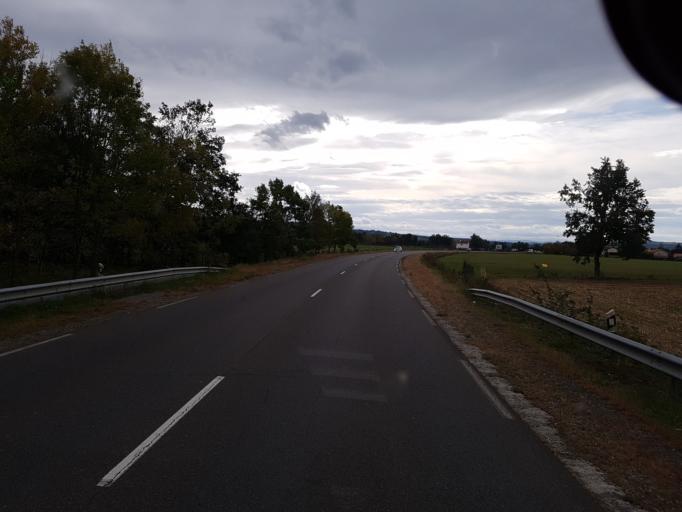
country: FR
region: Rhone-Alpes
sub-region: Departement de la Loire
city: Chamboeuf
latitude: 45.5667
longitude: 4.3101
